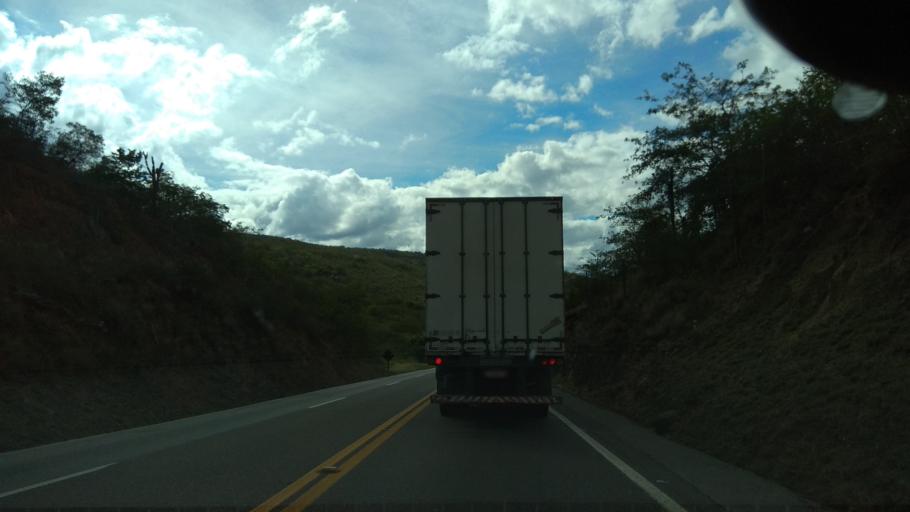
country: BR
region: Bahia
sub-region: Amargosa
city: Amargosa
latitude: -12.9012
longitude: -39.8612
